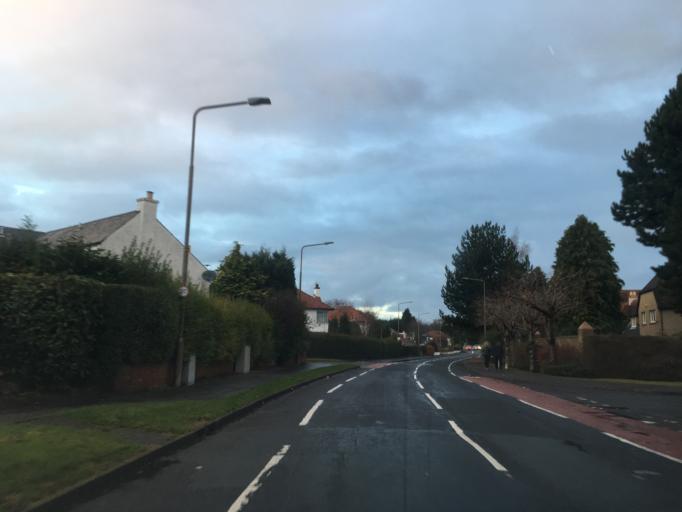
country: GB
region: Scotland
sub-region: Edinburgh
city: Colinton
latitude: 55.9596
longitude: -3.2701
